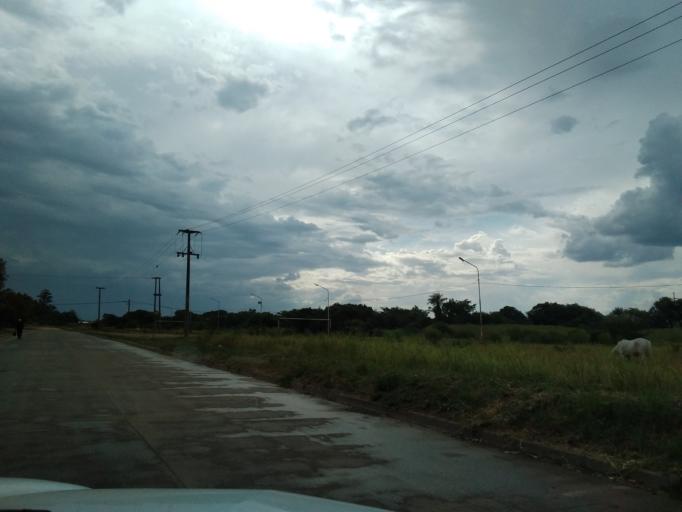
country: AR
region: Corrientes
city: Corrientes
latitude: -27.5177
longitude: -58.7904
